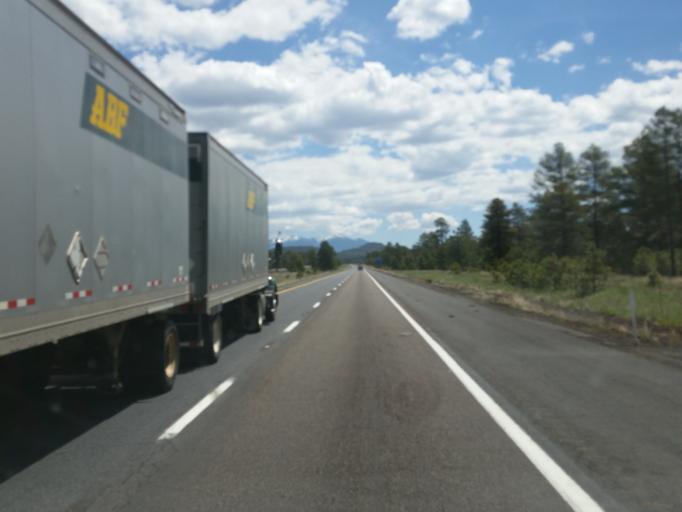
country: US
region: Arizona
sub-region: Coconino County
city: Parks
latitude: 35.2508
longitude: -111.9570
